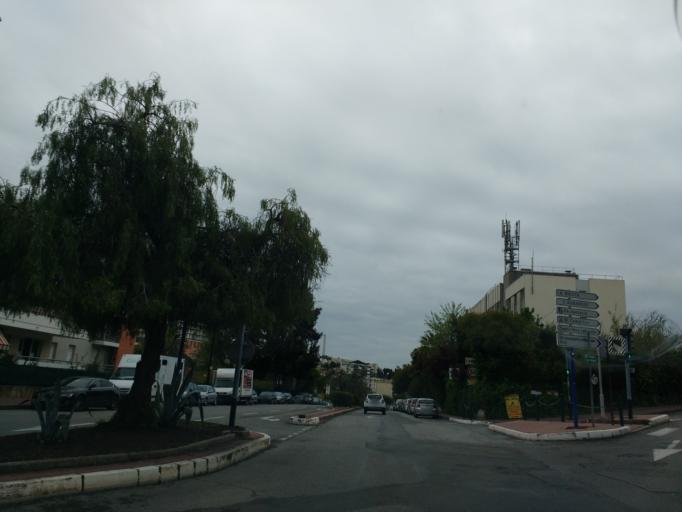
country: FR
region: Provence-Alpes-Cote d'Azur
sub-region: Departement des Alpes-Maritimes
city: Le Cannet
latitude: 43.5677
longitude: 7.0024
